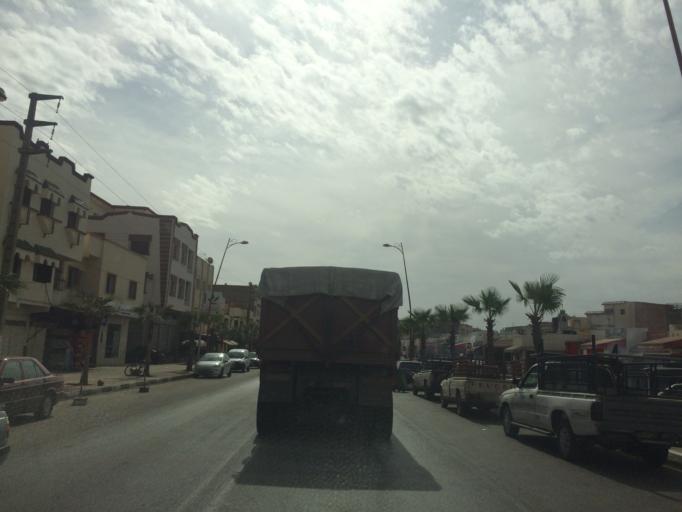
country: MA
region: Meknes-Tafilalet
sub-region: El-Hajeb
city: El Hajeb
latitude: 33.7593
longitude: -5.4855
